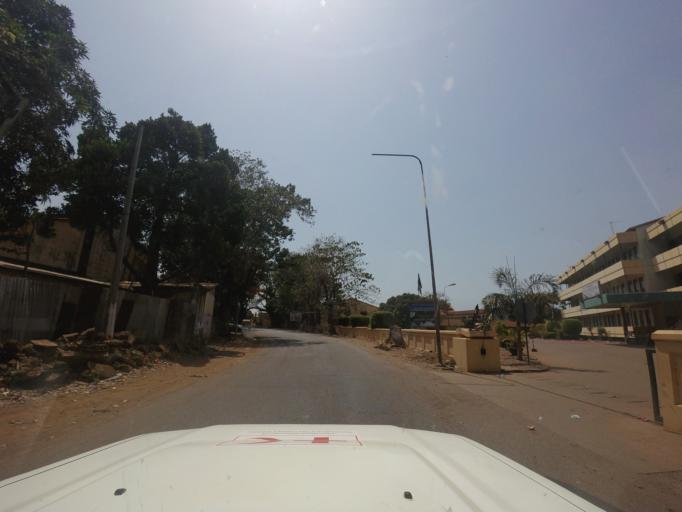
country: GN
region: Conakry
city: Camayenne
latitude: 9.5163
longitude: -13.7124
